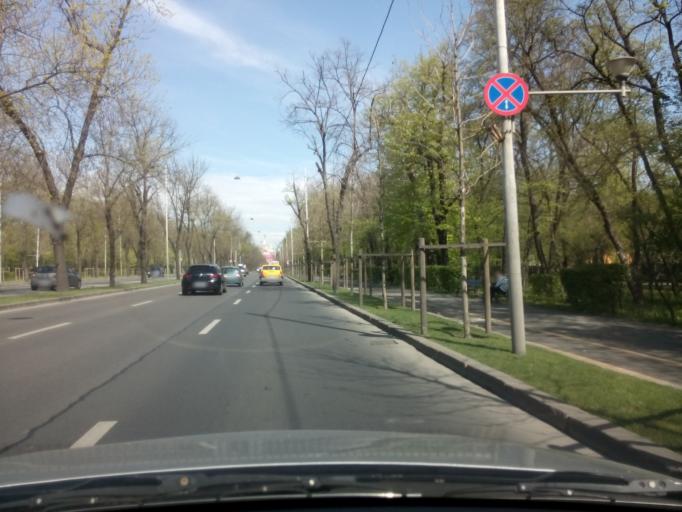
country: RO
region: Bucuresti
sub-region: Municipiul Bucuresti
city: Bucuresti
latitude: 44.4687
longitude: 26.0776
